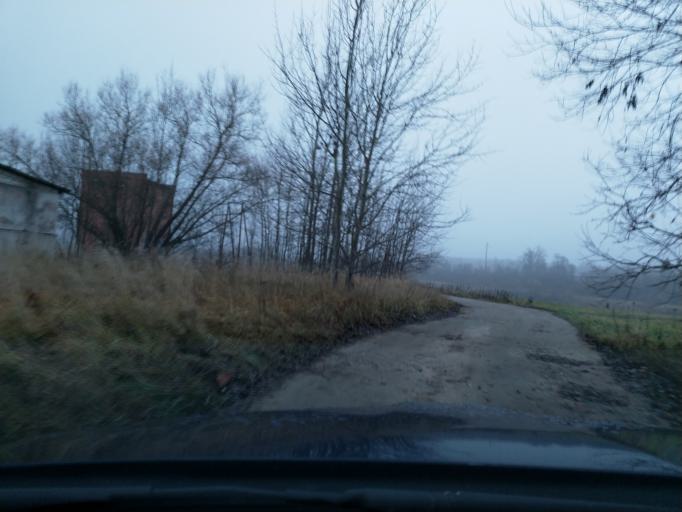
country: LV
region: Kuldigas Rajons
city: Kuldiga
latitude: 56.9795
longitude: 21.9696
